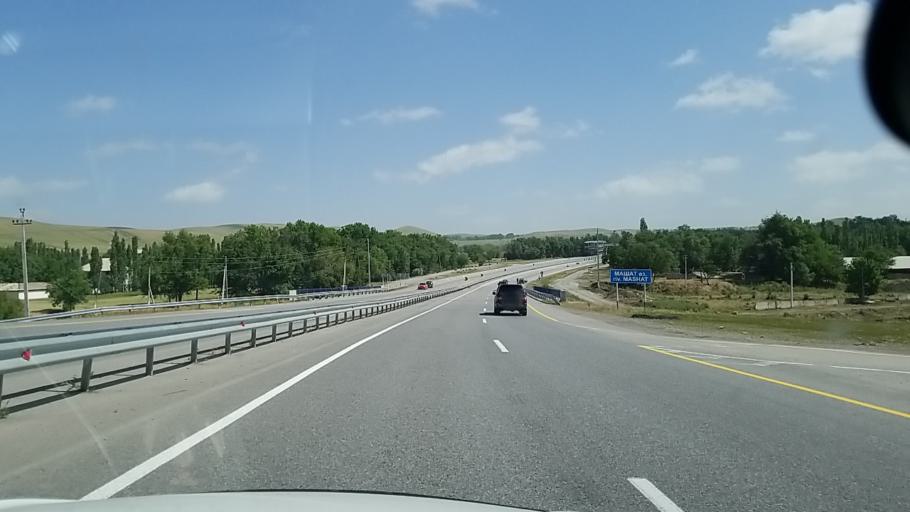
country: KZ
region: Ongtustik Qazaqstan
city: Sastobe
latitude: 42.4989
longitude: 69.9591
